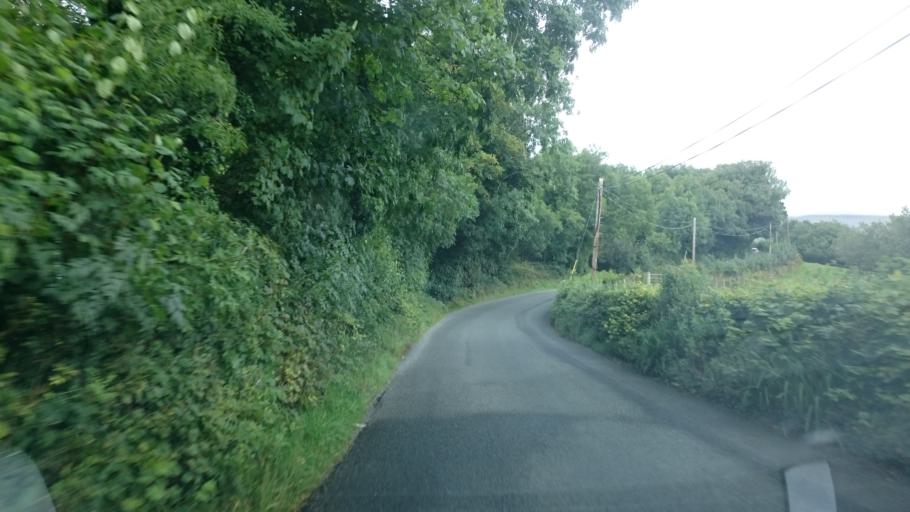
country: IE
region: Connaught
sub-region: Maigh Eo
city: Westport
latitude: 53.9039
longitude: -9.5505
